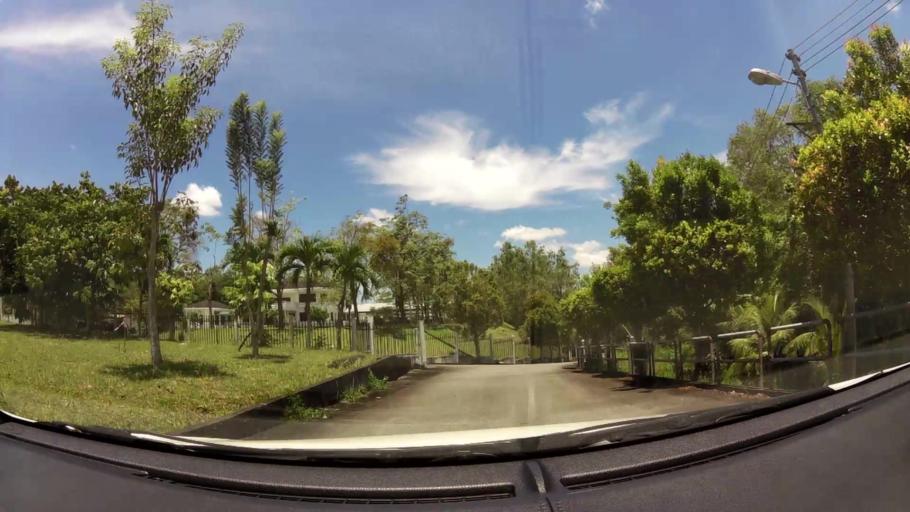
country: BN
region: Brunei and Muara
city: Bandar Seri Begawan
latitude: 4.9313
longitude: 114.9624
